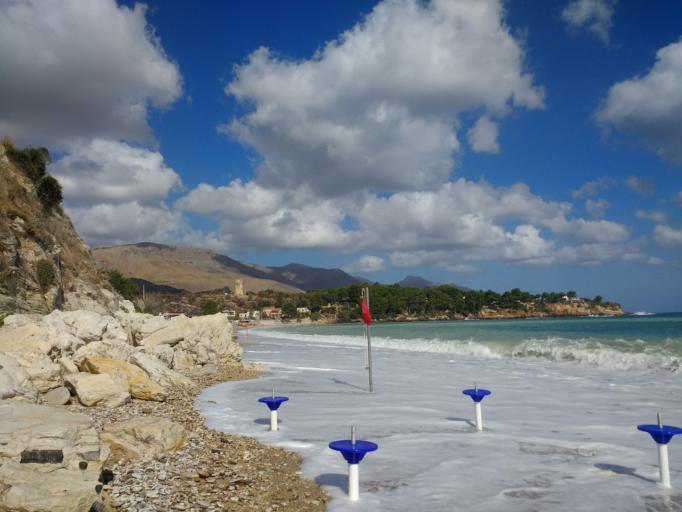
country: IT
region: Sicily
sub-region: Trapani
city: Castellammare del Golfo
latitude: 38.0554
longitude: 12.8429
